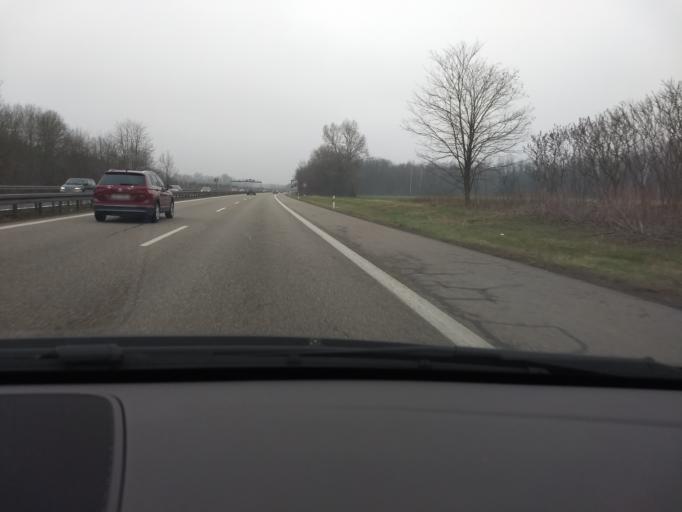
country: FR
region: Alsace
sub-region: Departement du Haut-Rhin
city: Rosenau
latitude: 47.6475
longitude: 7.5459
